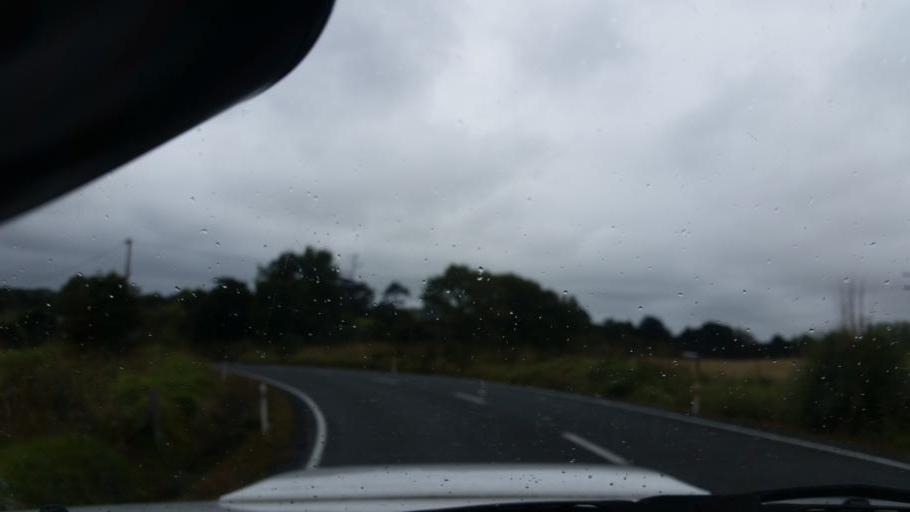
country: NZ
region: Auckland
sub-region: Auckland
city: Wellsford
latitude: -36.1411
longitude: 174.5050
